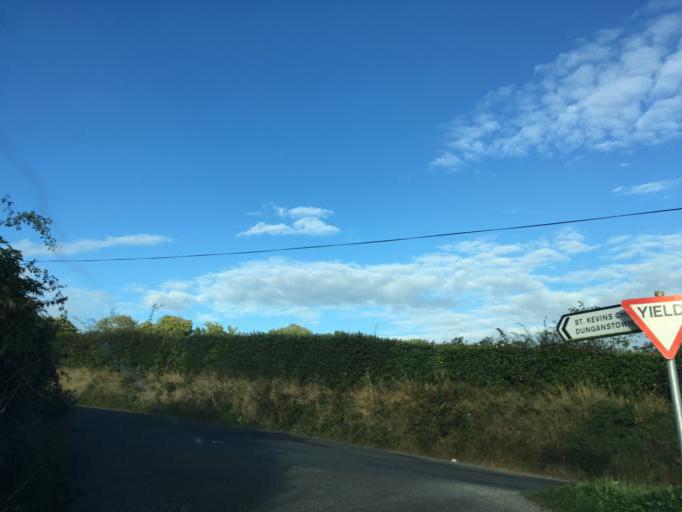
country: IE
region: Leinster
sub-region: Wicklow
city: Rathnew
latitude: 52.9229
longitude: -6.1080
